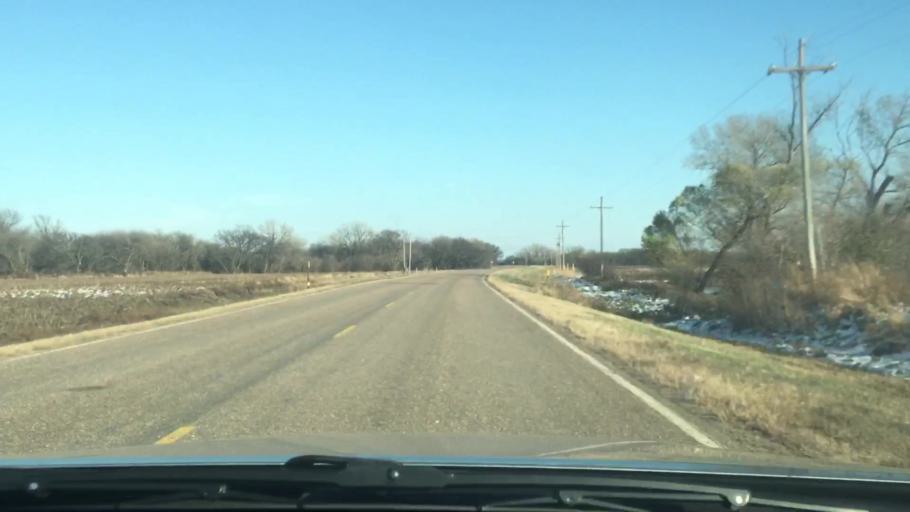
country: US
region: Kansas
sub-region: Rice County
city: Lyons
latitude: 38.2895
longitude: -98.1530
